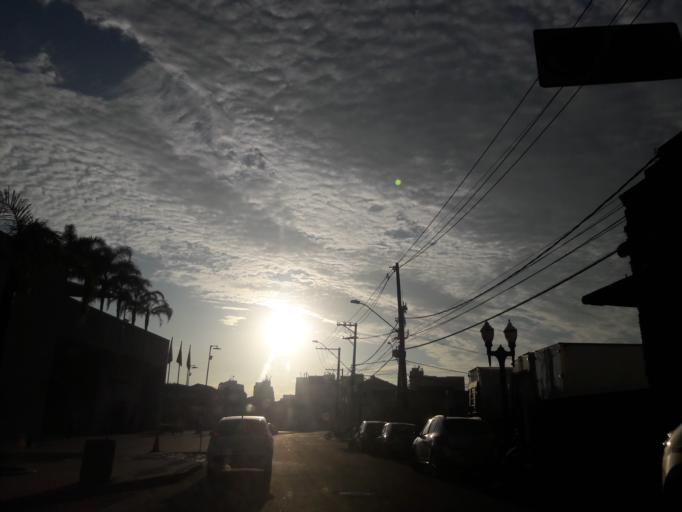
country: BR
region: Sao Paulo
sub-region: Santos
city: Santos
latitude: -23.9308
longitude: -46.3363
